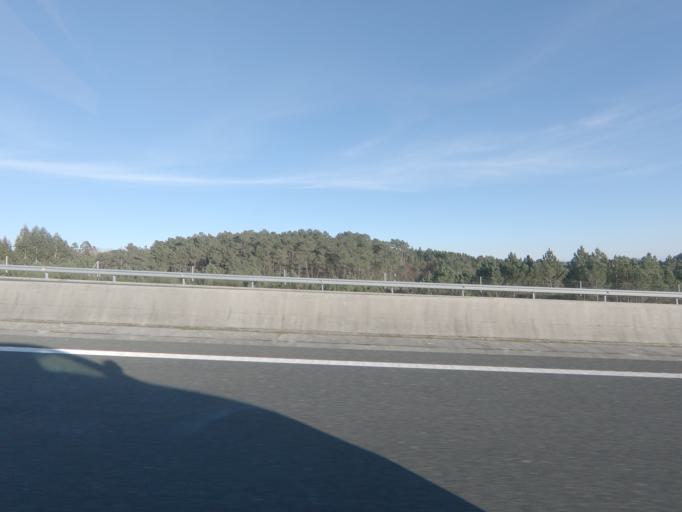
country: ES
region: Galicia
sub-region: Provincia de Ourense
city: Pinor
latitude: 42.5322
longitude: -8.0150
